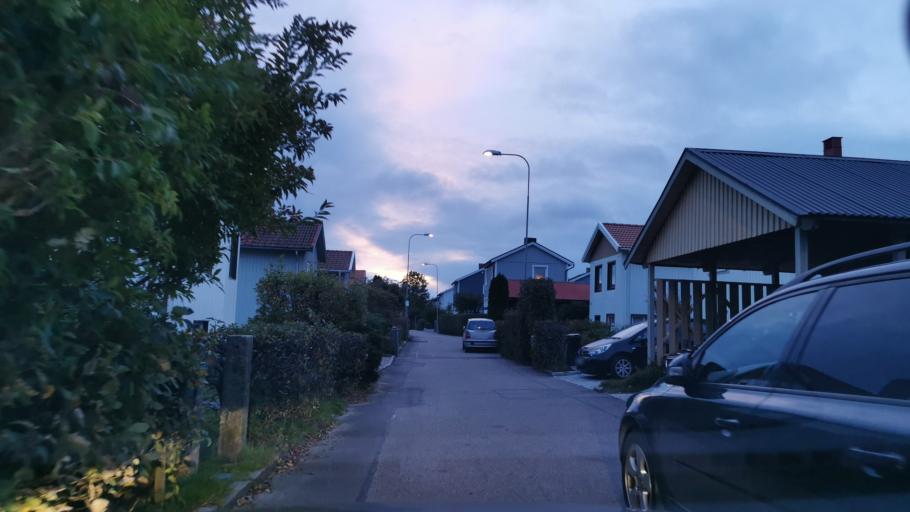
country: SE
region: Vaestra Goetaland
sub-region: Goteborg
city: Eriksbo
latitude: 57.7350
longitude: 12.0590
